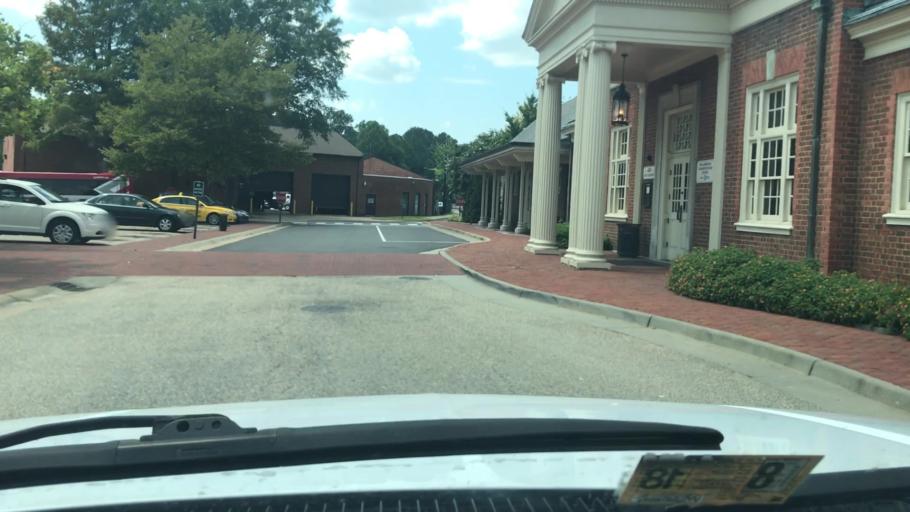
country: US
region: Virginia
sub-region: City of Williamsburg
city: Williamsburg
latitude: 37.2764
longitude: -76.7084
